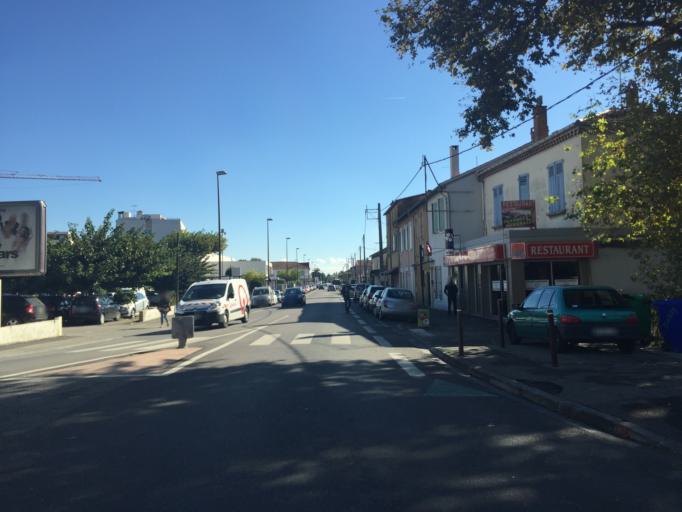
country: FR
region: Provence-Alpes-Cote d'Azur
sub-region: Departement du Vaucluse
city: Avignon
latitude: 43.9422
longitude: 4.8223
